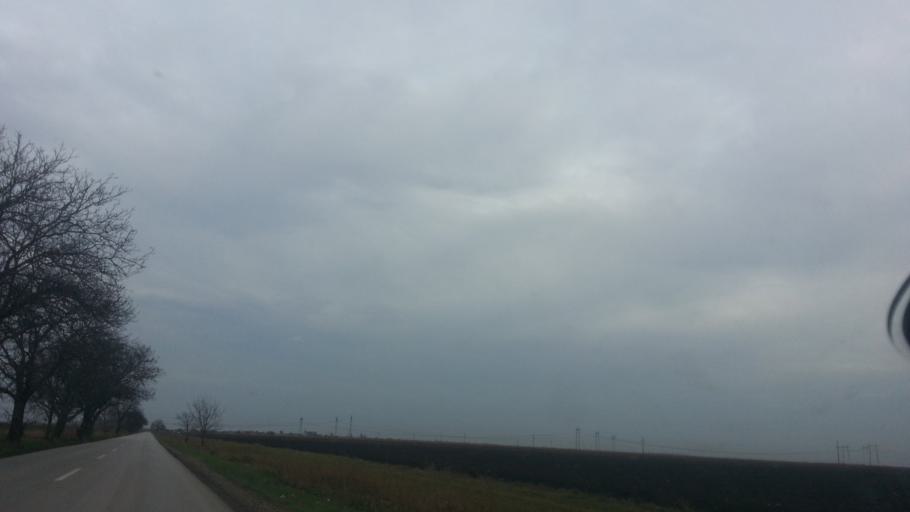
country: RS
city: Golubinci
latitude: 44.9800
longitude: 20.1004
